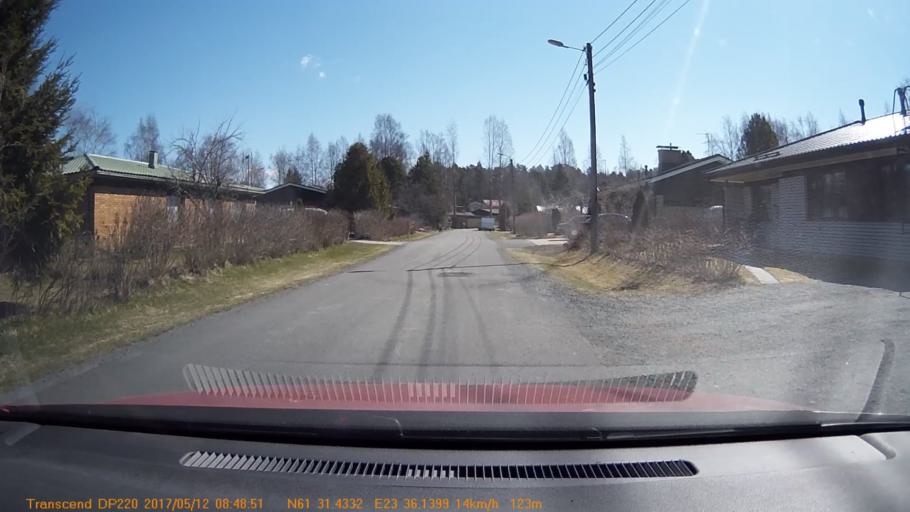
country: FI
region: Pirkanmaa
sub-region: Tampere
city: Yloejaervi
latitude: 61.5239
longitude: 23.6024
